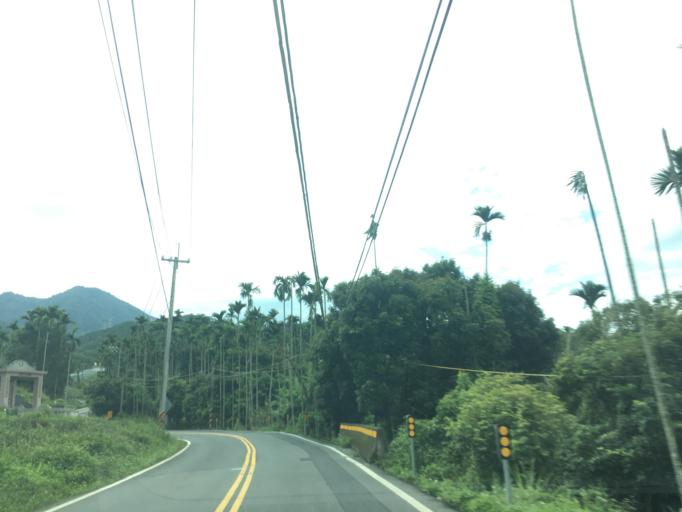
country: TW
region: Taiwan
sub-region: Yunlin
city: Douliu
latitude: 23.5689
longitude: 120.5668
